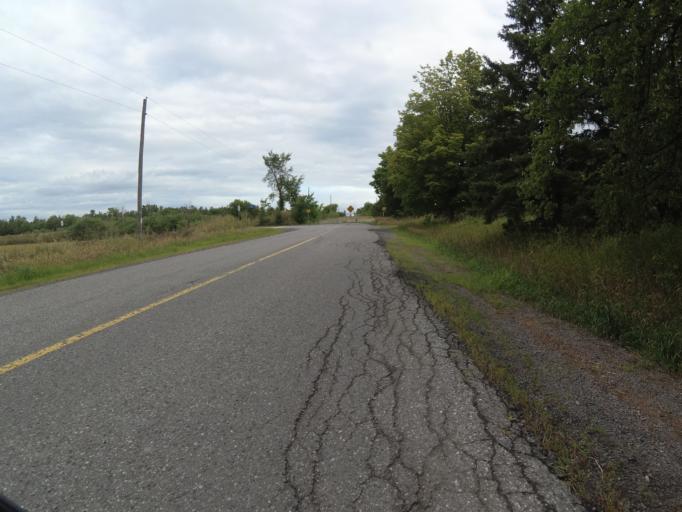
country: CA
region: Ontario
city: Clarence-Rockland
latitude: 45.4308
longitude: -75.3001
